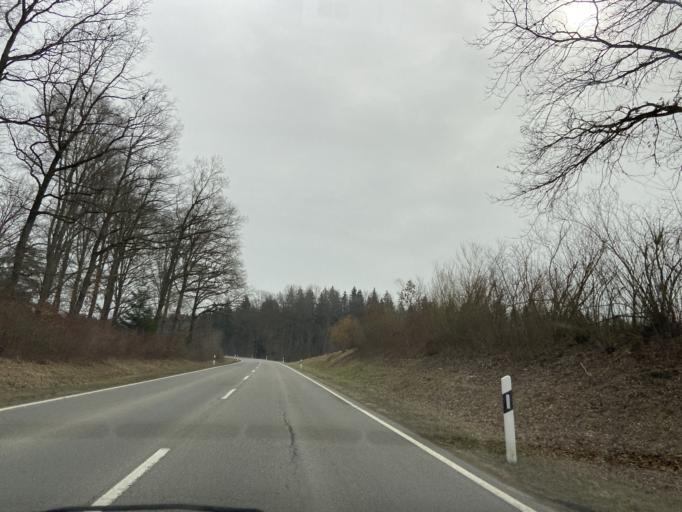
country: DE
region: Baden-Wuerttemberg
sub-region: Tuebingen Region
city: Krauchenwies
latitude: 48.0100
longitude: 9.2701
